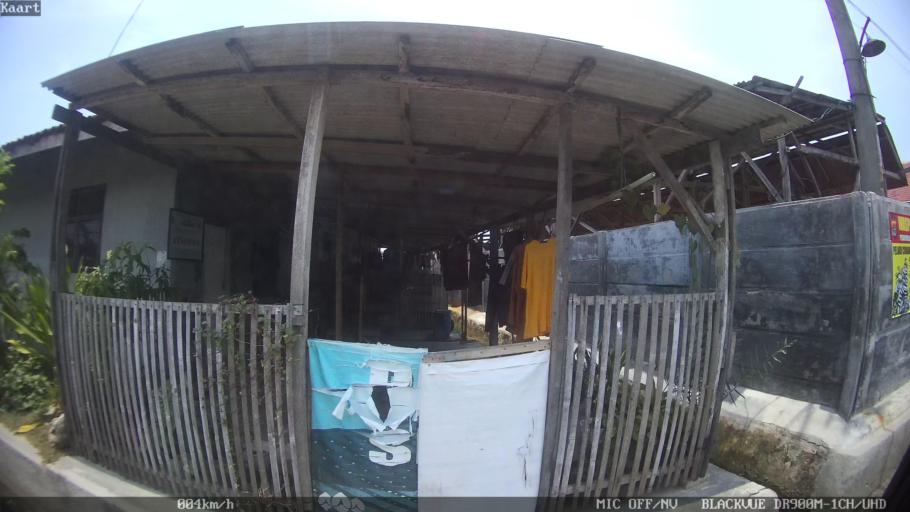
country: ID
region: Lampung
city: Bandarlampung
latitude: -5.4587
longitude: 105.2599
